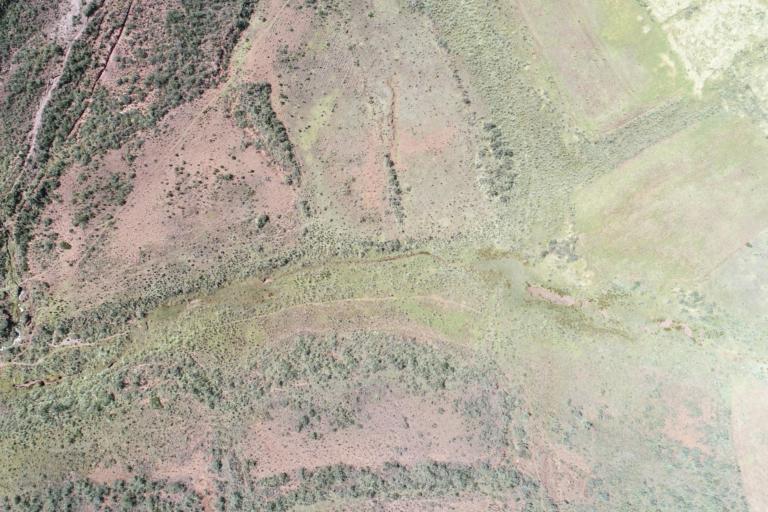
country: BO
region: La Paz
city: Tiahuanaco
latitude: -16.6060
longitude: -68.7731
